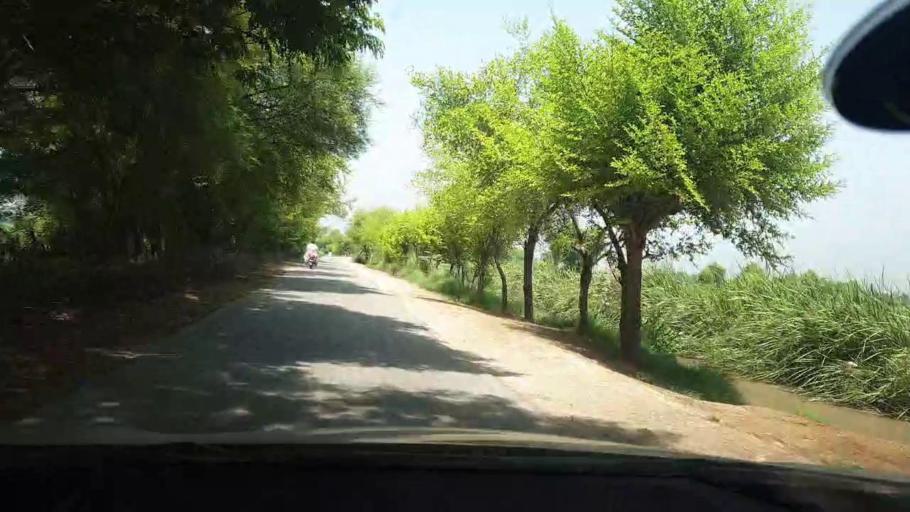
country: PK
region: Sindh
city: Kambar
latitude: 27.6416
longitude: 67.9739
